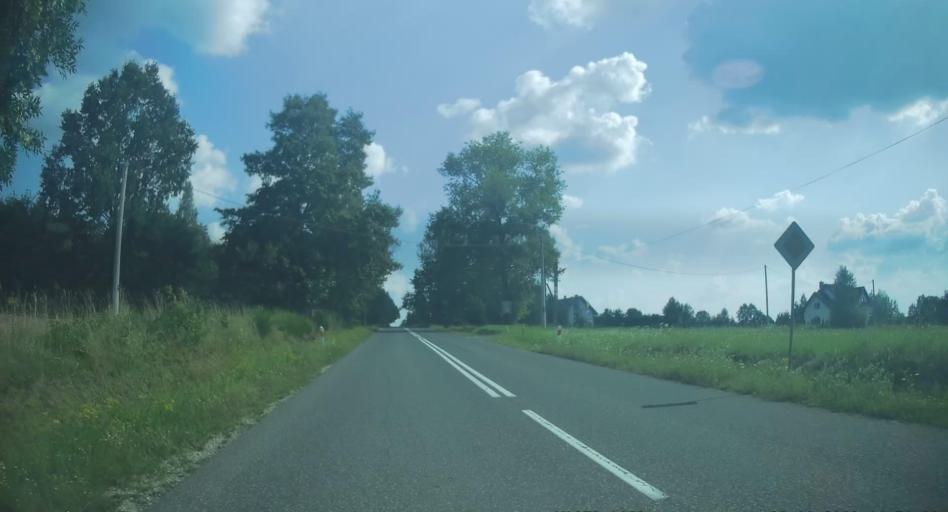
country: PL
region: Swietokrzyskie
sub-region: Powiat kielecki
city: Lopuszno
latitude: 50.9215
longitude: 20.2412
